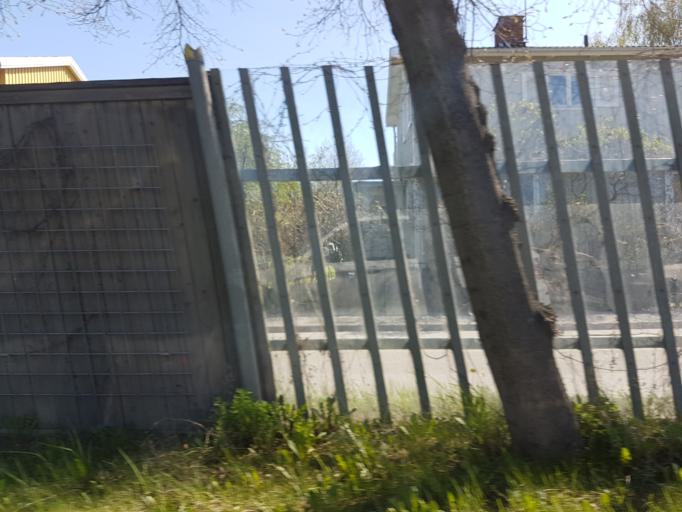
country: SE
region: Stockholm
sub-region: Stockholms Kommun
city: Bromma
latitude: 59.3343
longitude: 17.9275
